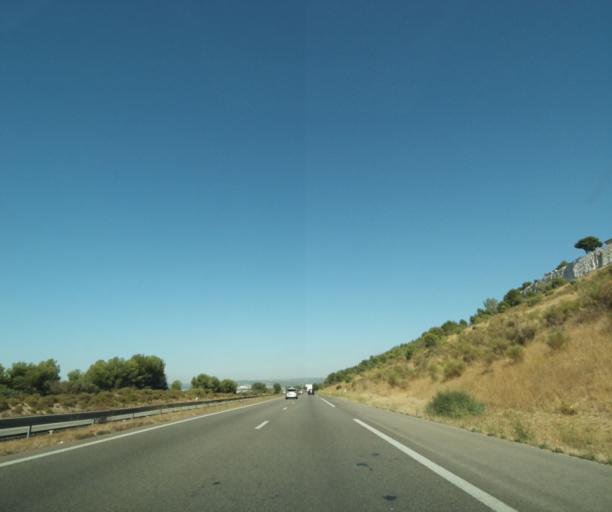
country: FR
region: Provence-Alpes-Cote d'Azur
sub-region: Departement des Bouches-du-Rhone
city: Vitrolles
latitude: 43.4620
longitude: 5.2349
